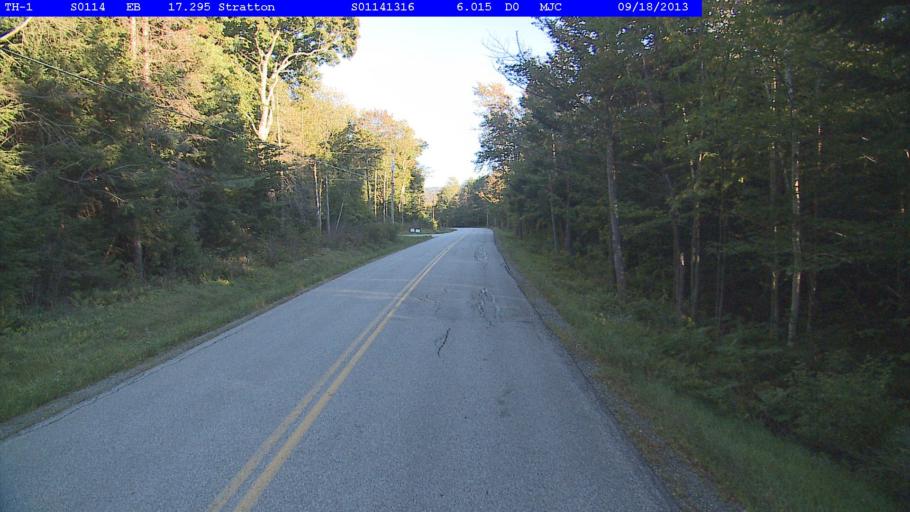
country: US
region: Vermont
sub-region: Windham County
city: Dover
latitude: 43.0365
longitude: -72.8974
